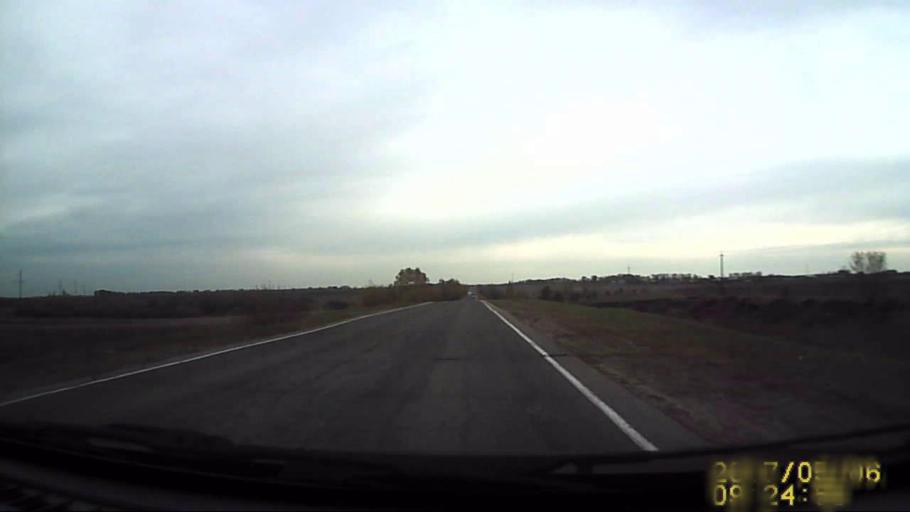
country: RU
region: Ulyanovsk
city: Cherdakly
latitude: 54.3809
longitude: 48.8136
